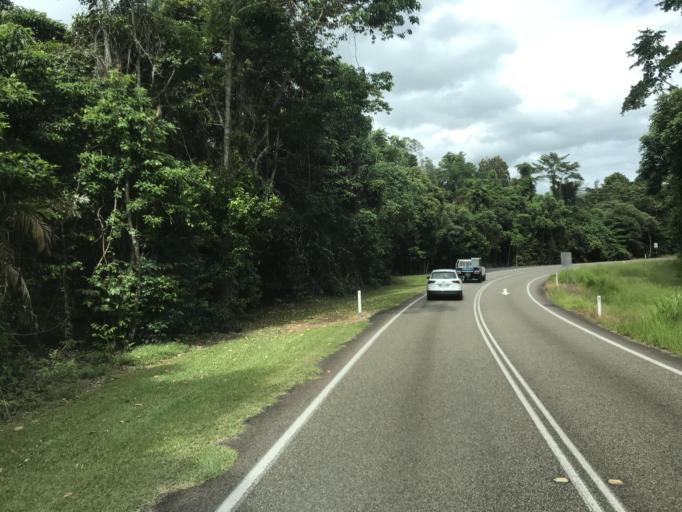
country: AU
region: Queensland
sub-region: Cassowary Coast
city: Innisfail
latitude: -17.8677
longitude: 146.0690
